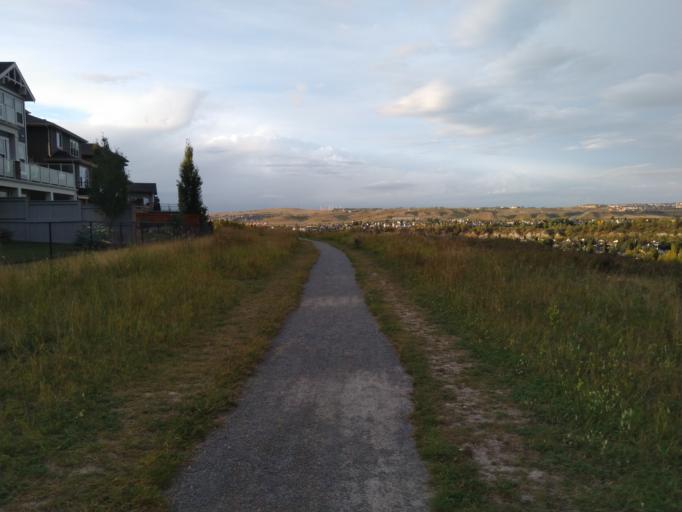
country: CA
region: Alberta
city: Cochrane
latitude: 51.1819
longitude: -114.5018
